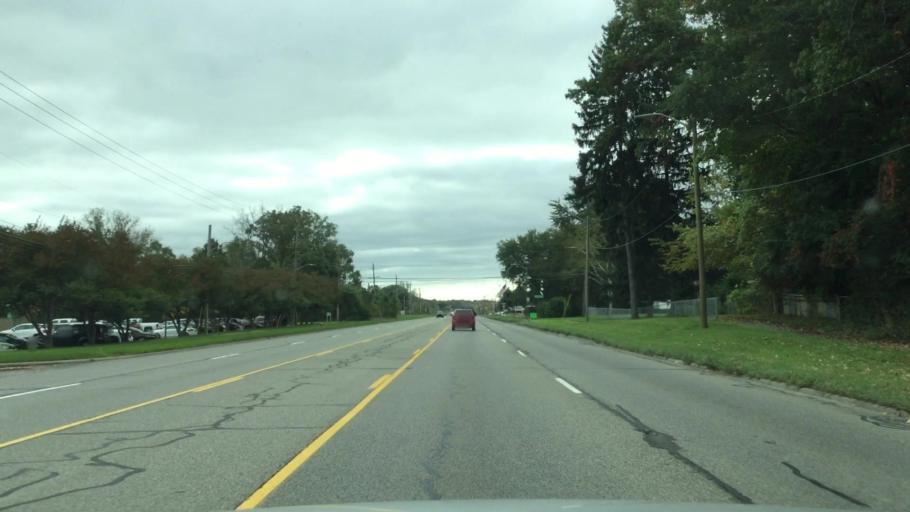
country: US
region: Michigan
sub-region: Oakland County
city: Keego Harbor
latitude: 42.6506
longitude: -83.3675
